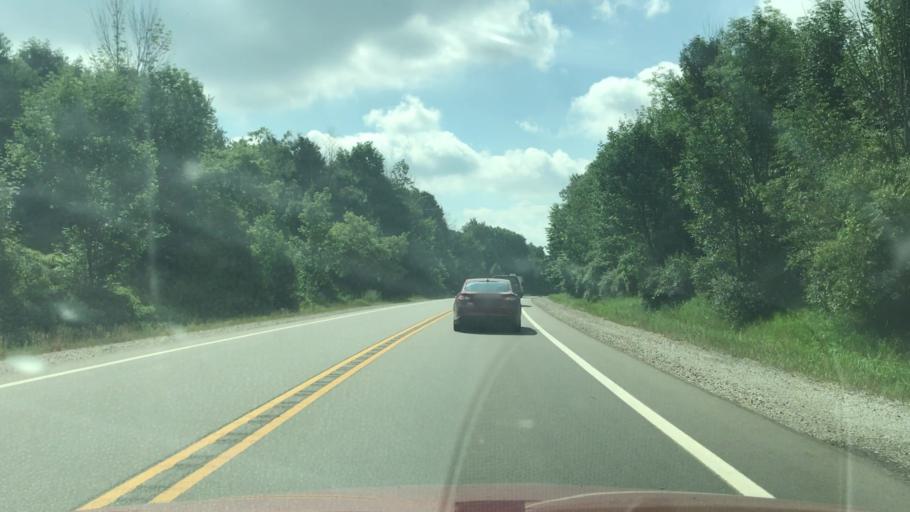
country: US
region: Michigan
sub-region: Kent County
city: Kent City
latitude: 43.1984
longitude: -85.7252
